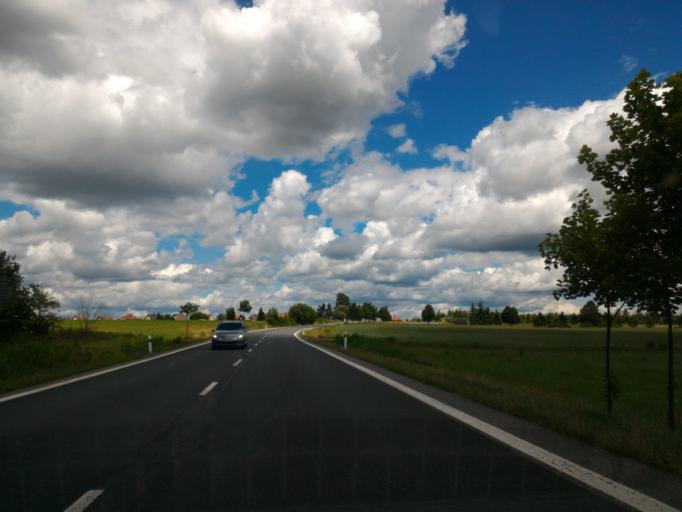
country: CZ
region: Vysocina
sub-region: Okres Zd'ar nad Sazavou
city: Nove Veseli
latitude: 49.5115
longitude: 15.9008
